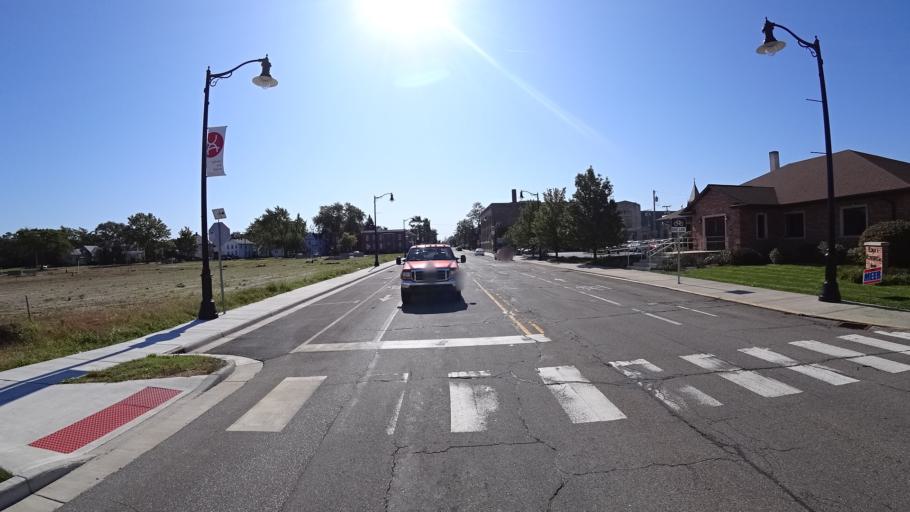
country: US
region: Indiana
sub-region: LaPorte County
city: Michigan City
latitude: 41.7176
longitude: -86.9003
